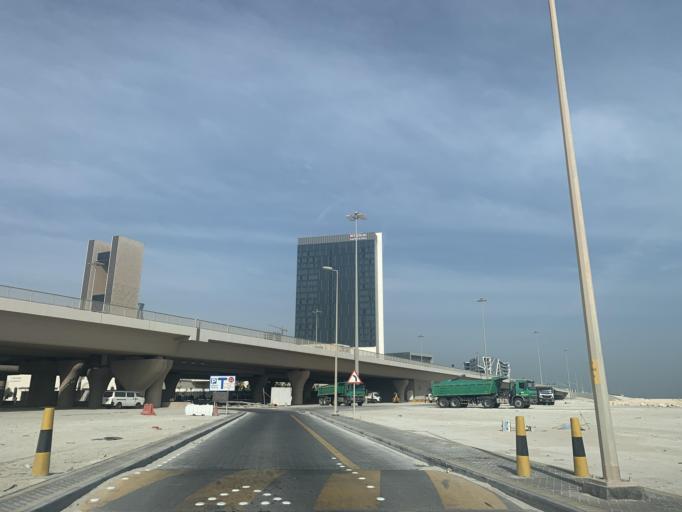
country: BH
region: Muharraq
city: Al Muharraq
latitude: 26.2486
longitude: 50.5888
